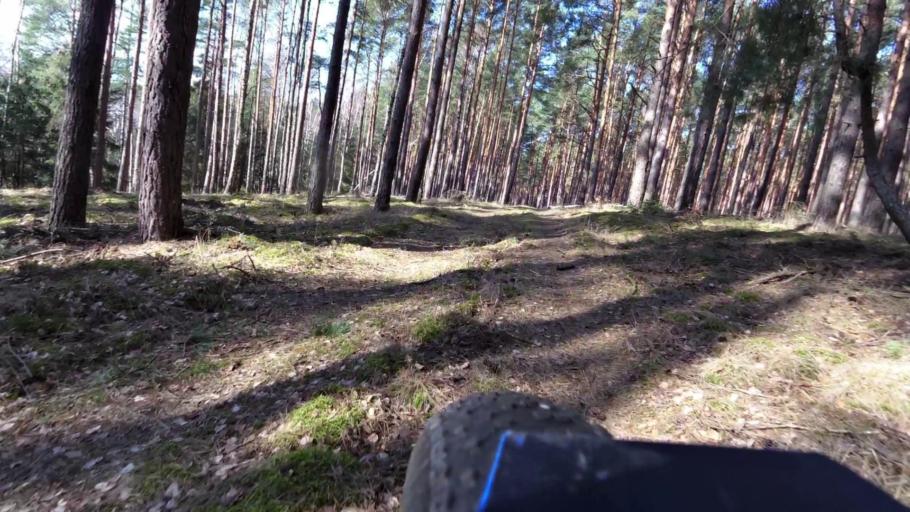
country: PL
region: Lubusz
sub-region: Powiat slubicki
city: Cybinka
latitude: 52.2090
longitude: 14.9238
